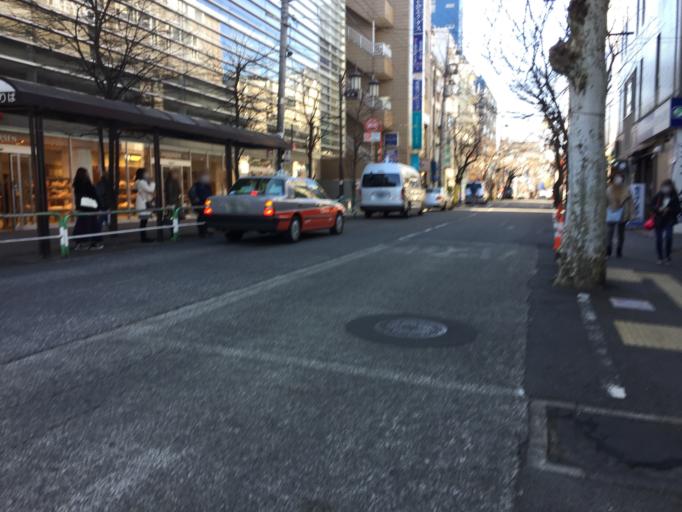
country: JP
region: Tokyo
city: Chofugaoka
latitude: 35.6405
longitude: 139.5989
